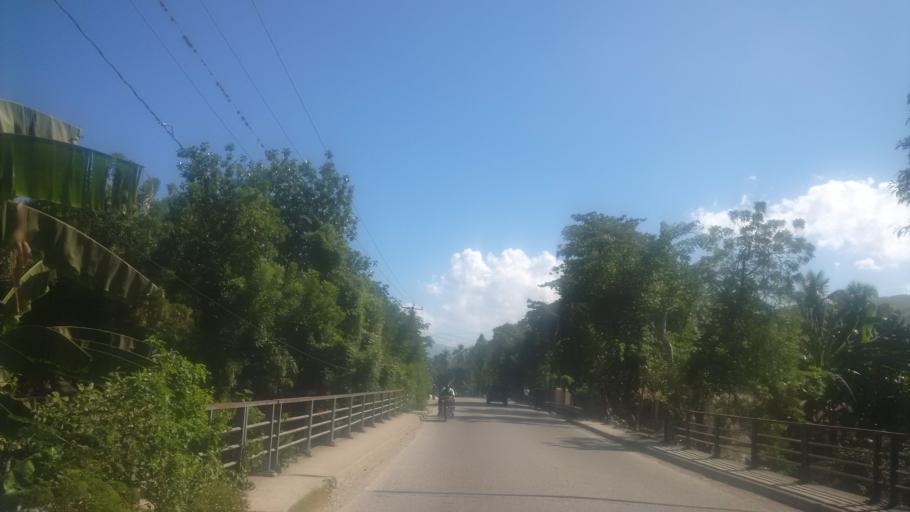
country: HT
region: Ouest
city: Tigwav
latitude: 18.4208
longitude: -72.9207
